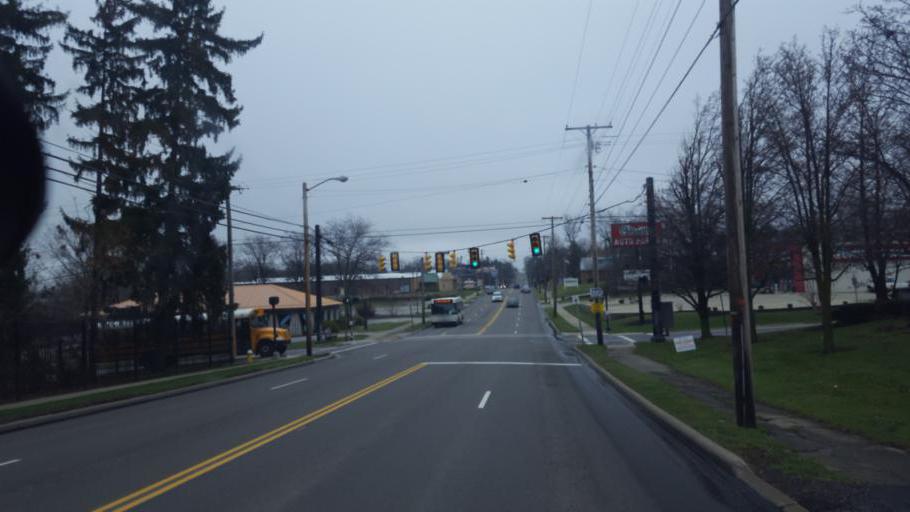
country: US
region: Ohio
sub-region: Richland County
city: Mansfield
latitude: 40.7591
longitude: -82.5474
